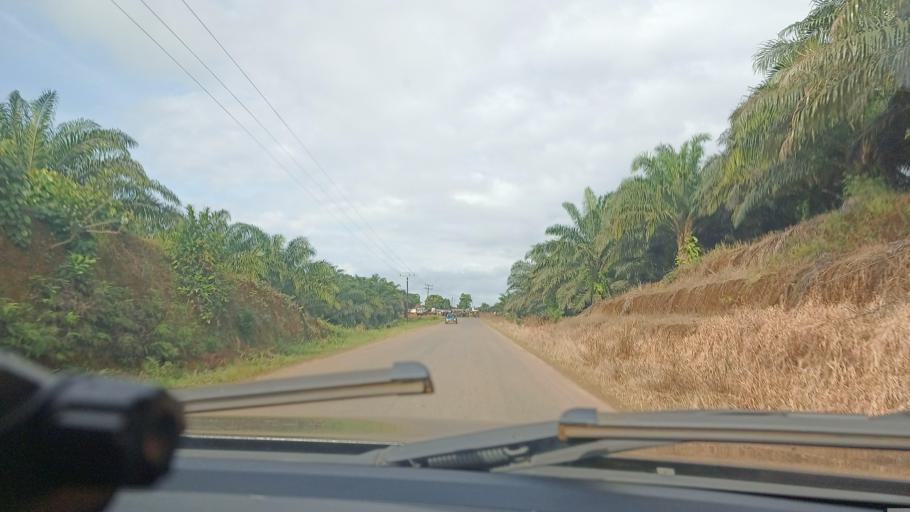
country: LR
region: Bomi
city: Tubmanburg
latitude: 6.7125
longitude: -10.9656
